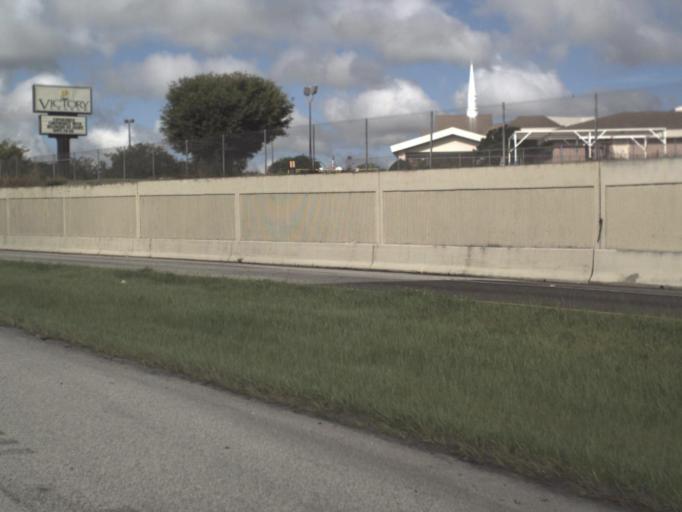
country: US
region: Florida
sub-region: Polk County
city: Gibsonia
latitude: 28.0827
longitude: -81.9741
